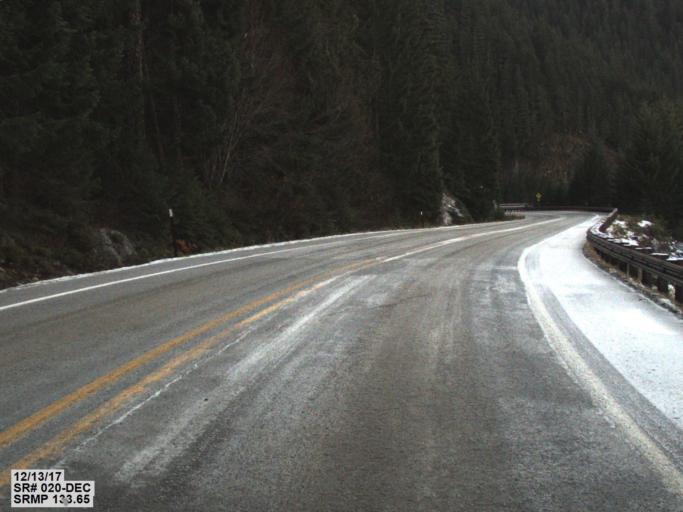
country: US
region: Washington
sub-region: Snohomish County
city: Darrington
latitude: 48.7221
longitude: -121.0676
